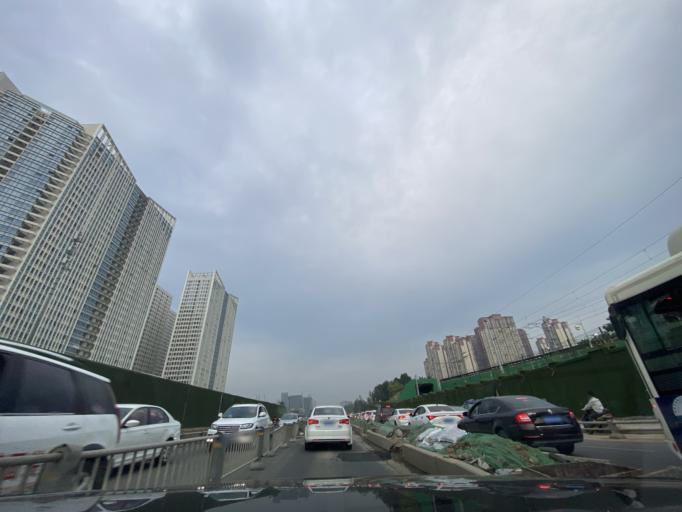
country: CN
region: Sichuan
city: Longquan
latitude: 30.6502
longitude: 104.2214
